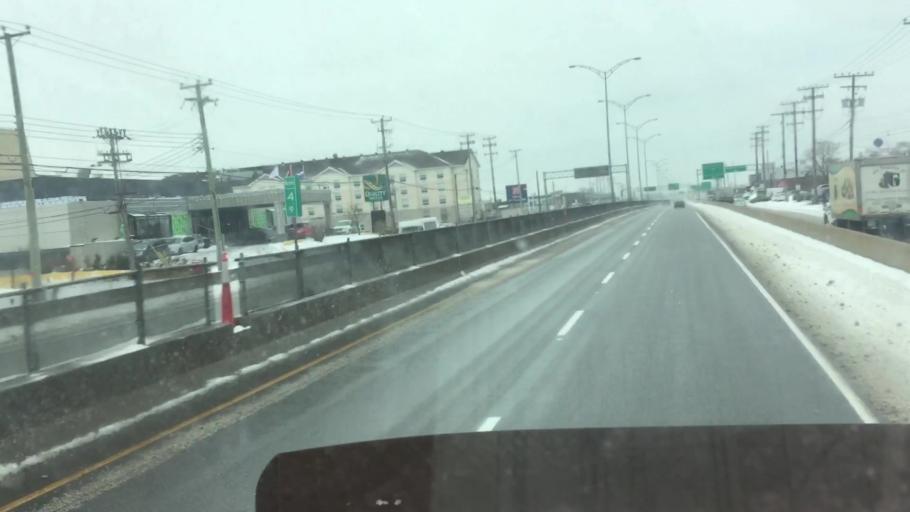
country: CA
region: Quebec
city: Cote-Saint-Luc
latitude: 45.4790
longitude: -73.7007
